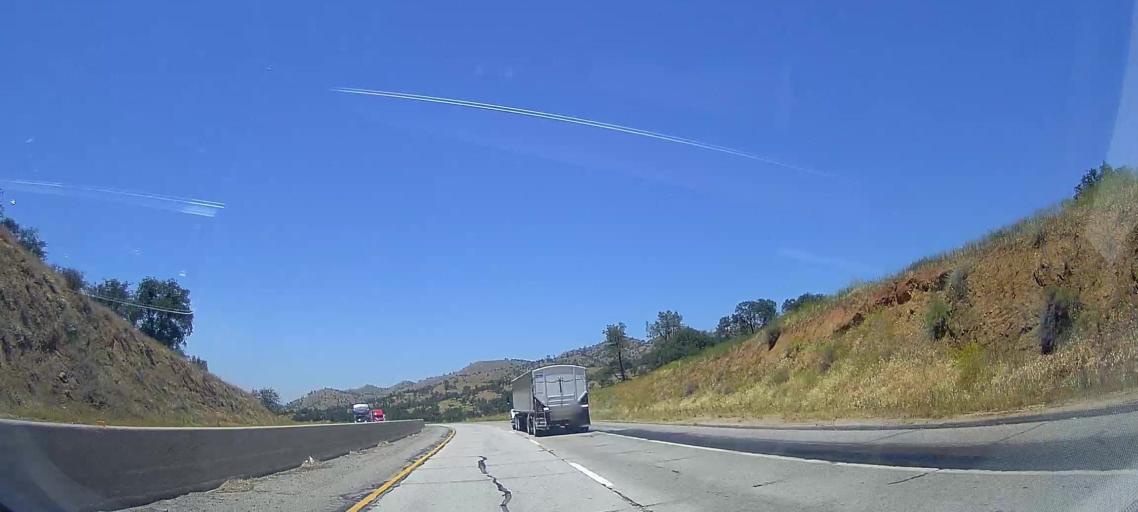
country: US
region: California
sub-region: Kern County
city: Golden Hills
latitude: 35.1883
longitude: -118.5048
